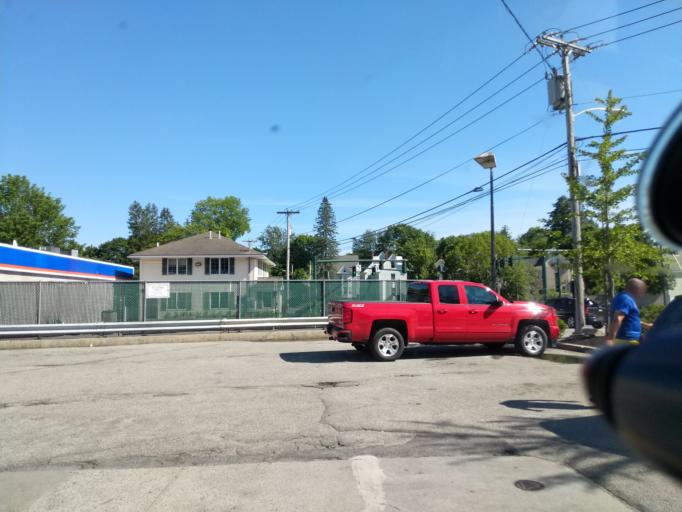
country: US
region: Maine
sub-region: Cumberland County
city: Westbrook
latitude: 43.6768
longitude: -70.3606
